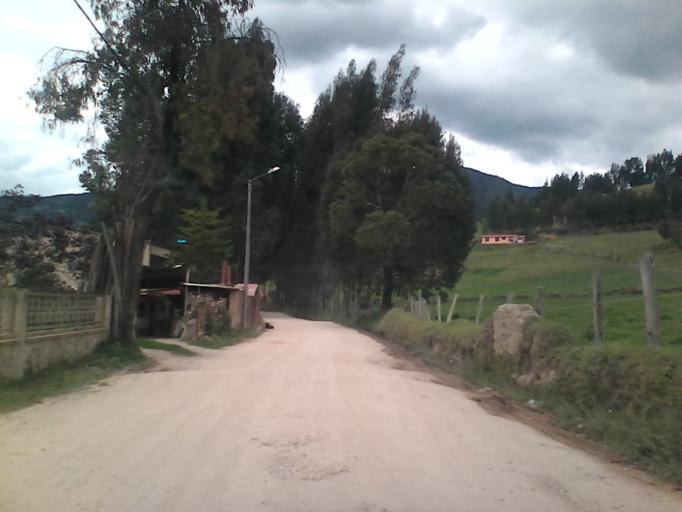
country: CO
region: Boyaca
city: Duitama
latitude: 5.8277
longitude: -73.0723
